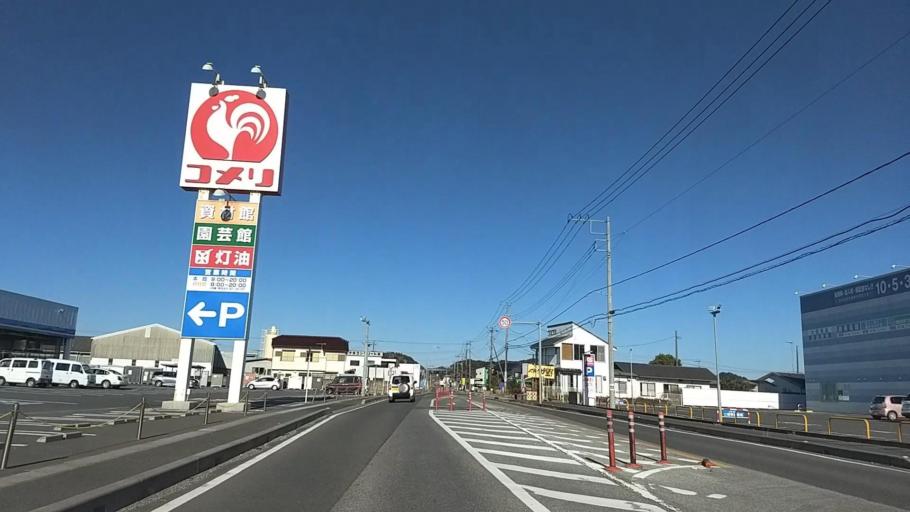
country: JP
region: Chiba
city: Ohara
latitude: 35.3017
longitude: 140.3988
